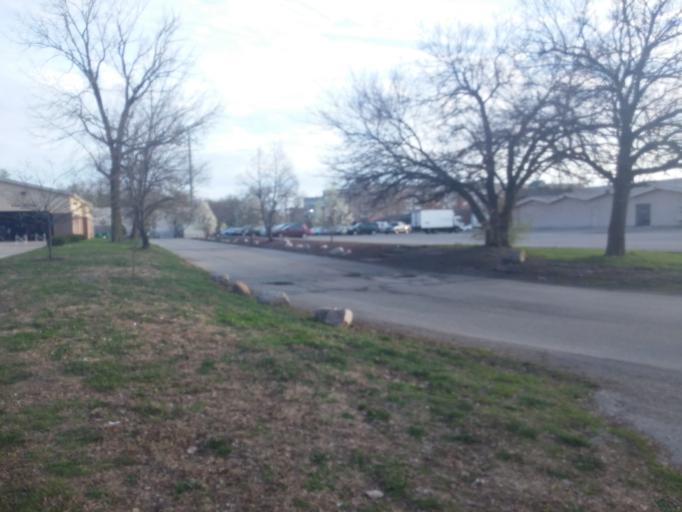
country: US
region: Indiana
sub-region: Tippecanoe County
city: West Lafayette
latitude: 40.4238
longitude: -86.8984
